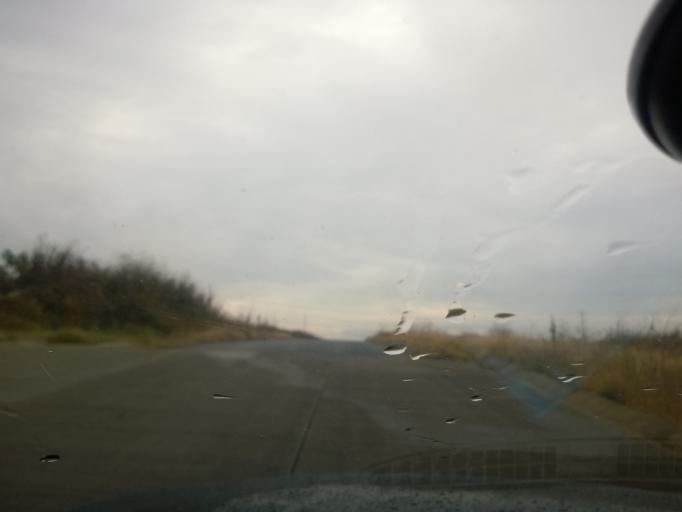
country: MX
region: Guanajuato
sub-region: Leon
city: La Ermita
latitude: 21.1561
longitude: -101.7347
